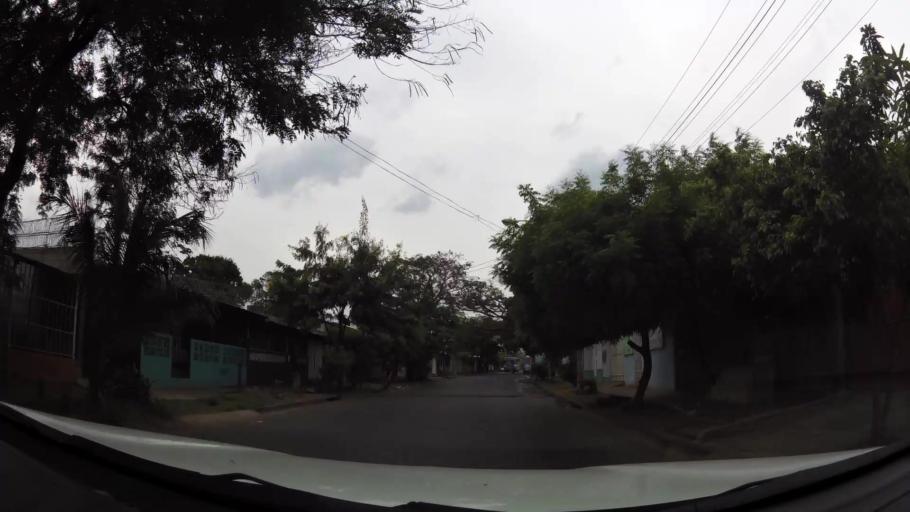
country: NI
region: Managua
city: Managua
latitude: 12.1215
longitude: -86.2268
